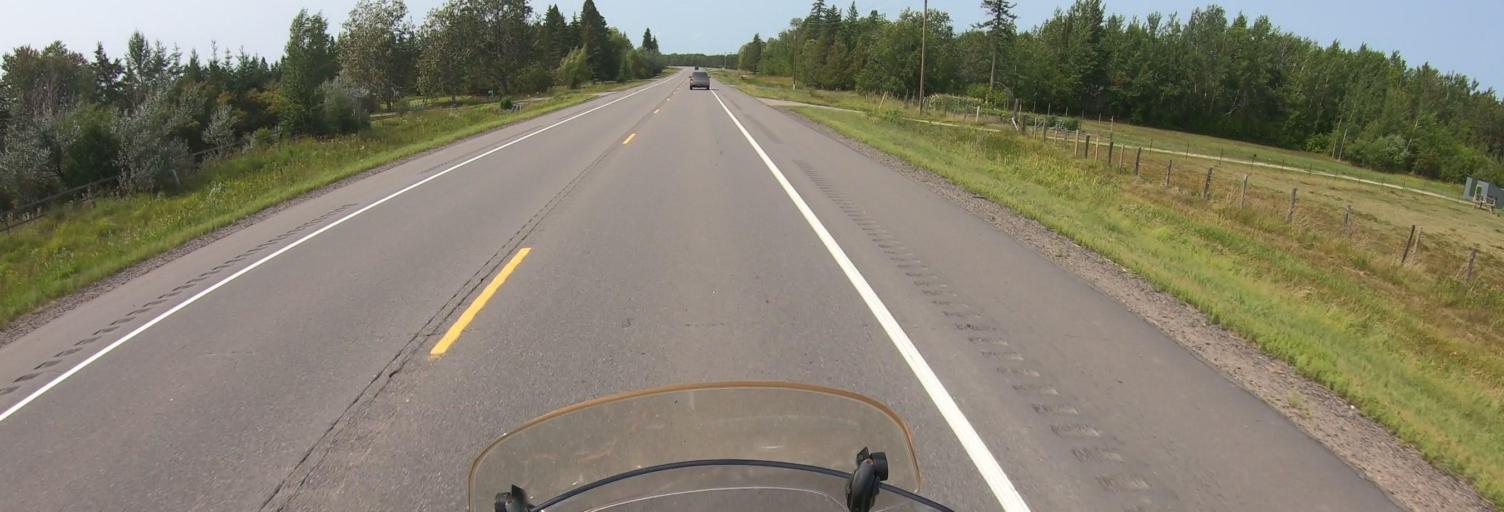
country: US
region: Minnesota
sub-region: Koochiching County
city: International Falls
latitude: 48.5344
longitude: -93.4974
